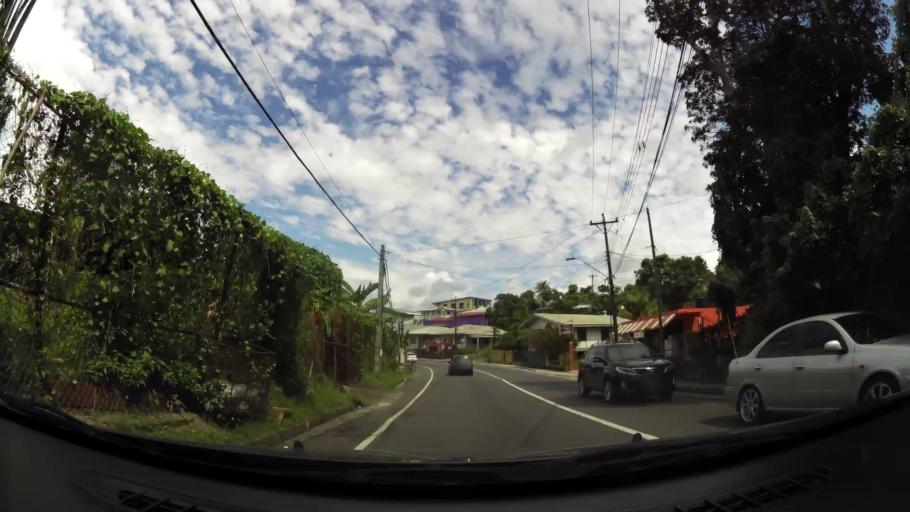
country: TT
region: City of San Fernando
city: San Fernando
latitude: 10.2879
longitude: -61.4562
